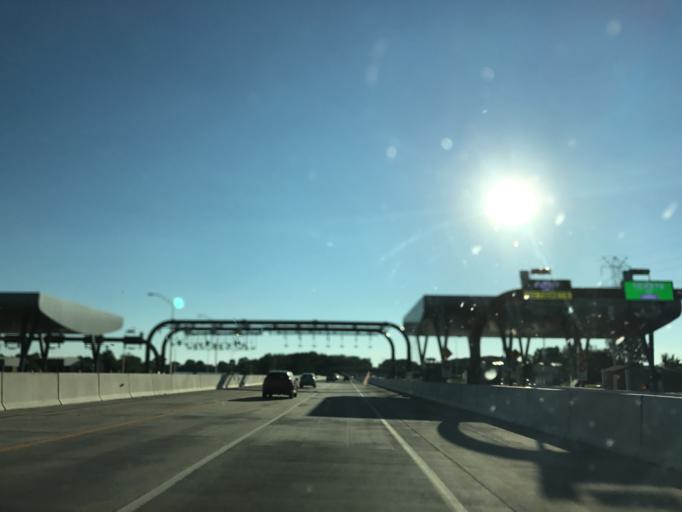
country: US
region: Pennsylvania
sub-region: Bucks County
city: Trevose
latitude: 40.1281
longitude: -74.9469
